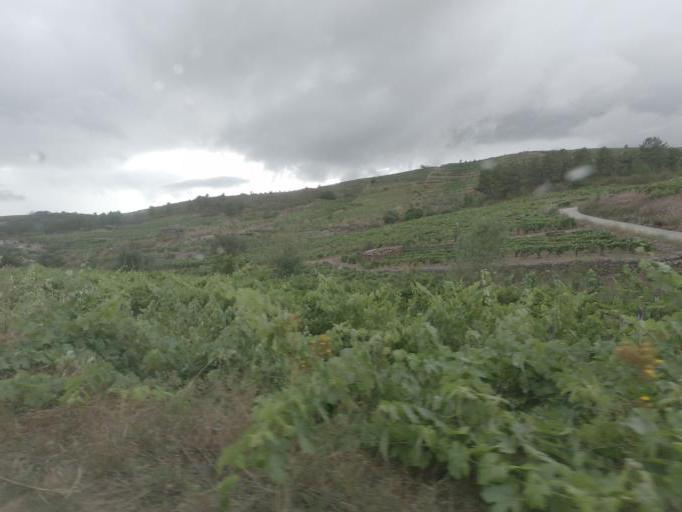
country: PT
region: Vila Real
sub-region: Sabrosa
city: Sabrosa
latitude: 41.2346
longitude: -7.4950
